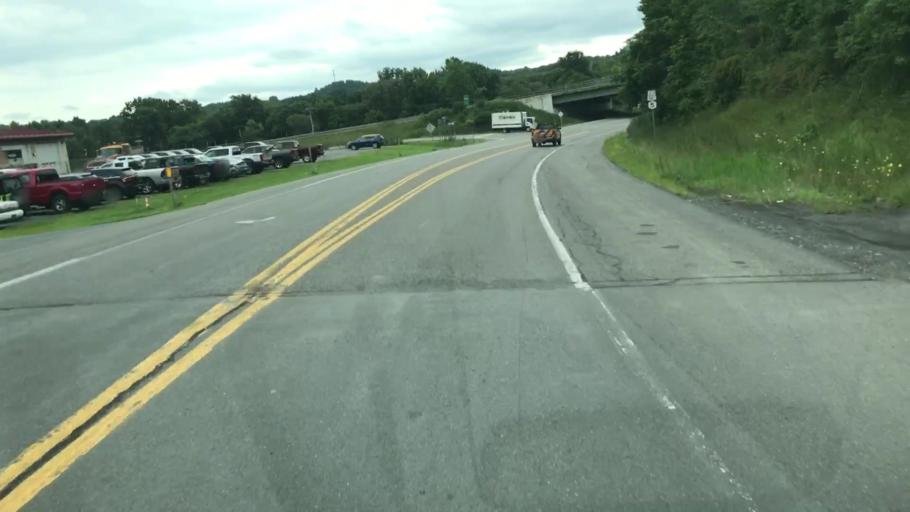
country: US
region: New York
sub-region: Onondaga County
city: Camillus
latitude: 43.0503
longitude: -76.3057
